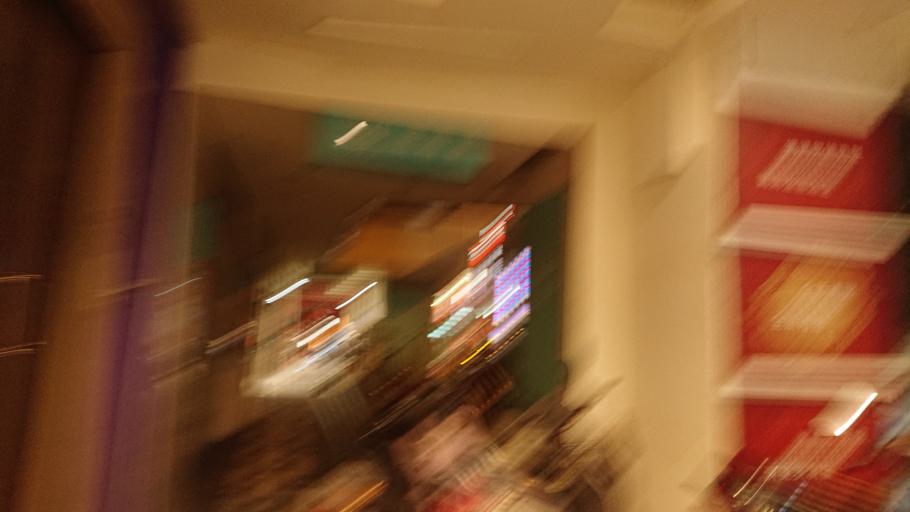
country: TW
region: Taiwan
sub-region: Tainan
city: Tainan
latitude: 22.9935
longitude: 120.2027
